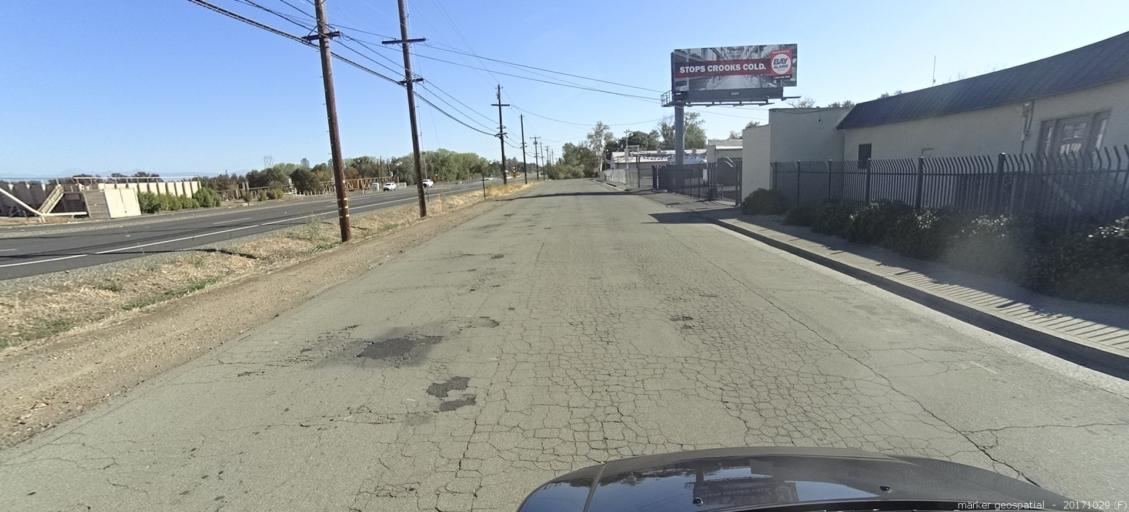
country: US
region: California
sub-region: Shasta County
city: Anderson
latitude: 40.4687
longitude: -122.3286
